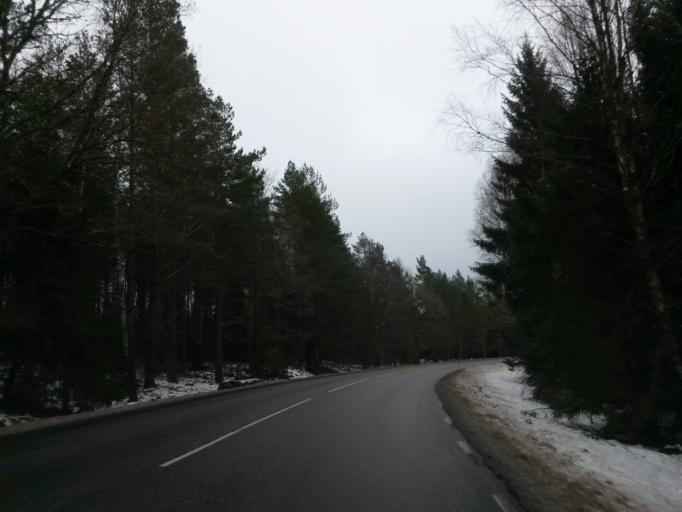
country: SE
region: Vaestra Goetaland
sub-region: Vargarda Kommun
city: Vargarda
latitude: 57.9887
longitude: 12.8358
